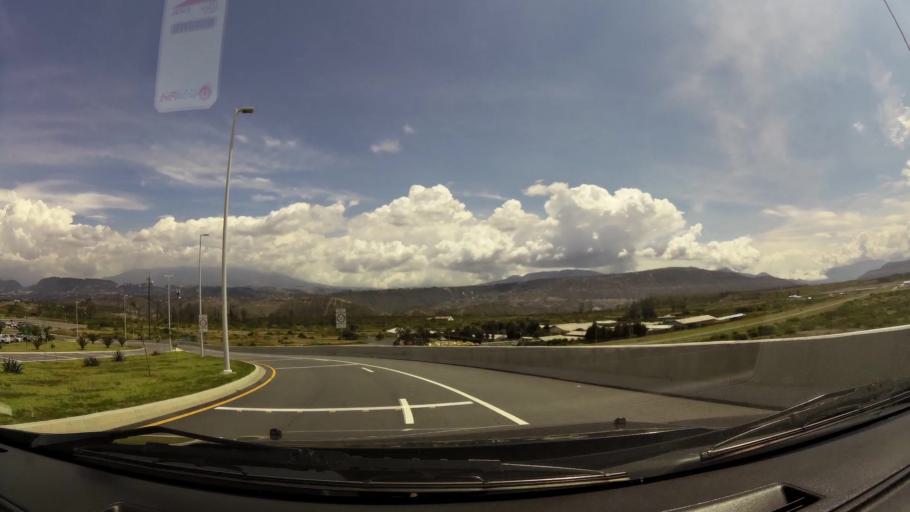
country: EC
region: Pichincha
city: Quito
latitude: -0.1228
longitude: -78.3614
